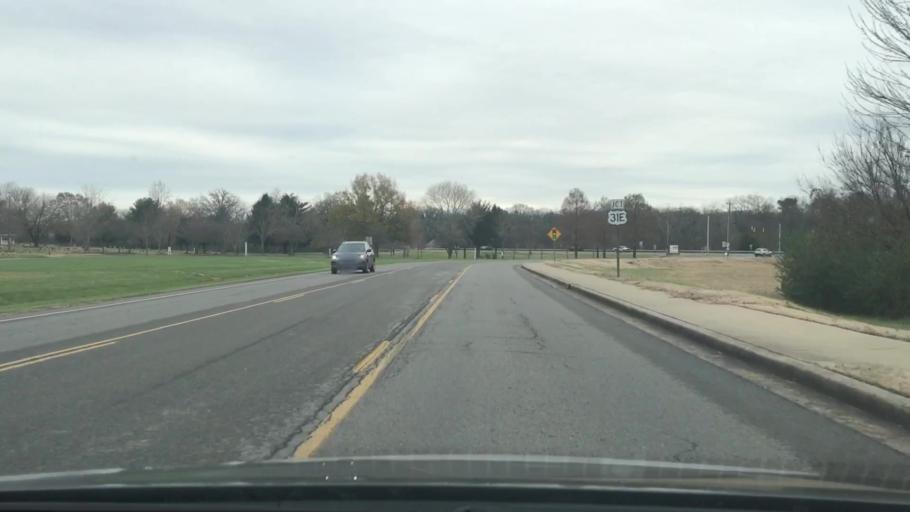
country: US
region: Tennessee
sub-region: Sumner County
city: Gallatin
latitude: 36.4036
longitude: -86.4332
